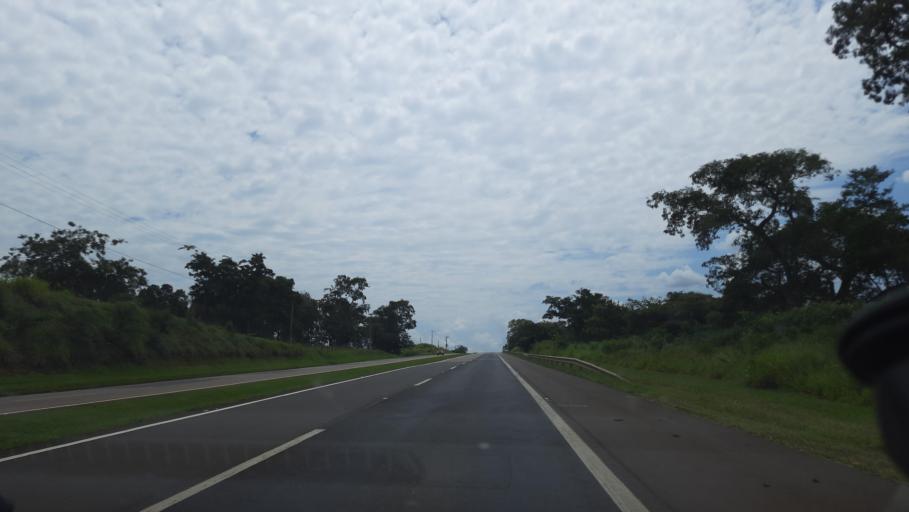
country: BR
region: Sao Paulo
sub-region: Casa Branca
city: Casa Branca
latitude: -21.7273
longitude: -47.0769
